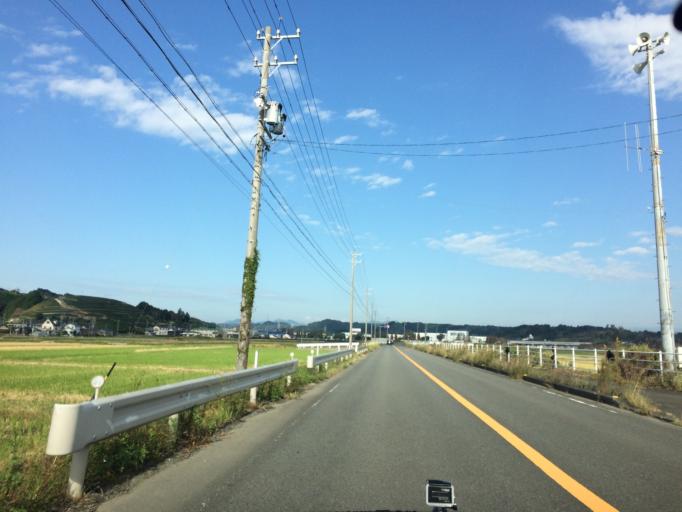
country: JP
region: Shizuoka
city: Shimada
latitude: 34.7663
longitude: 138.2359
